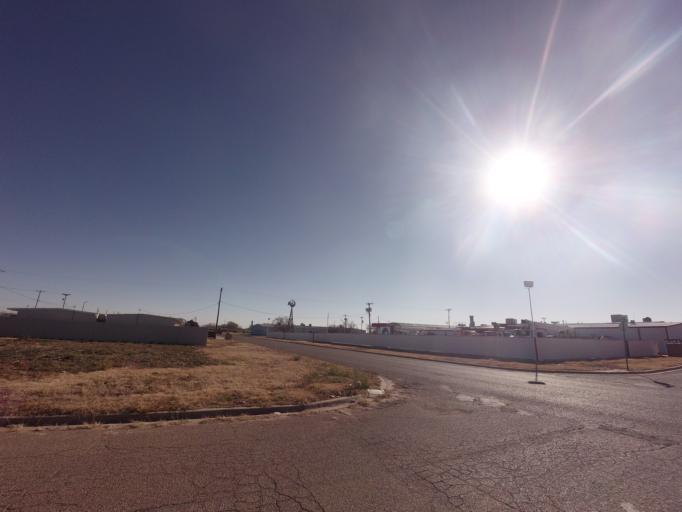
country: US
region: New Mexico
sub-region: Curry County
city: Clovis
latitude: 34.3998
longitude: -103.1902
